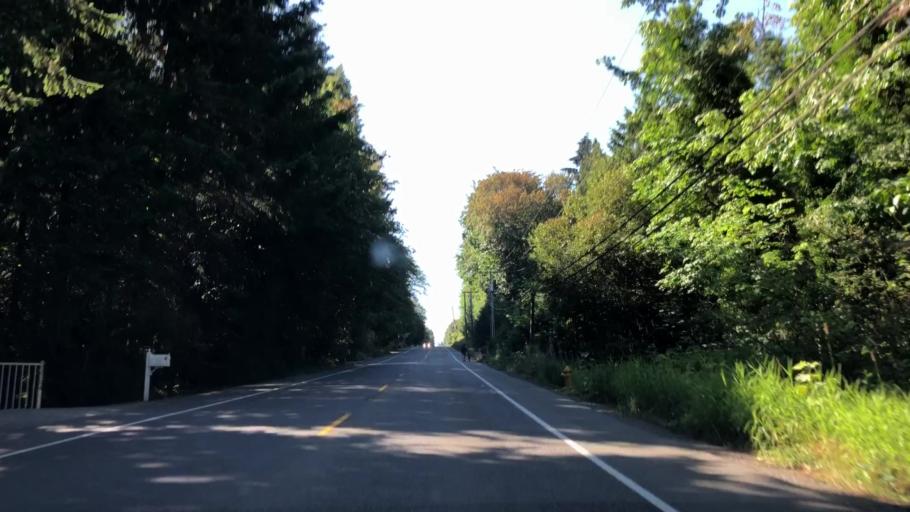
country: US
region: Washington
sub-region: Kitsap County
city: Kingston
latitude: 47.7906
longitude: -122.5051
